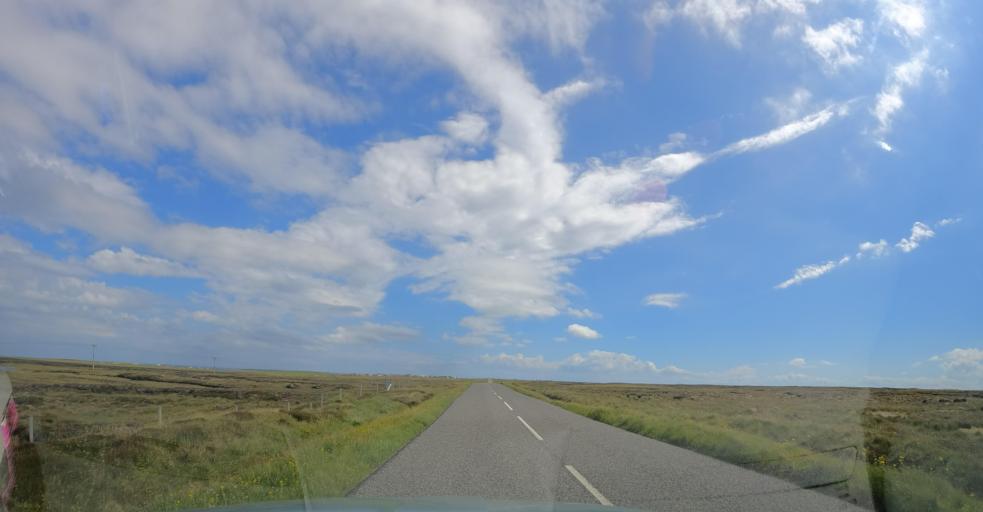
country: GB
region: Scotland
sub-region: Eilean Siar
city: Isle of Lewis
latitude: 58.4596
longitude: -6.3323
